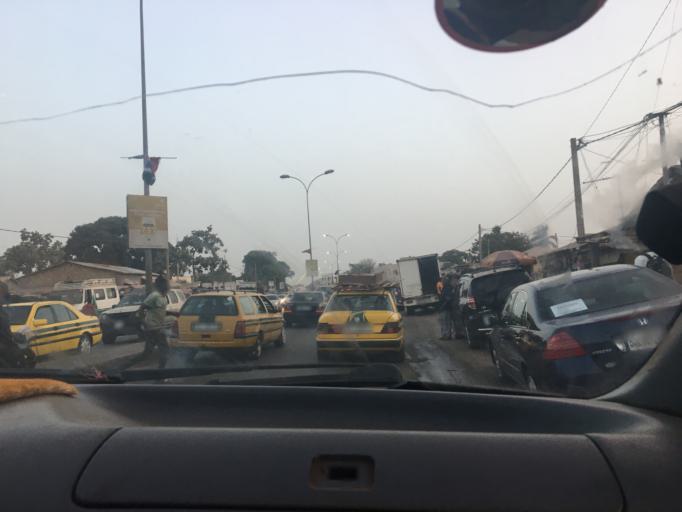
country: GM
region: Banjul
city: Bakau
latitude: 13.4396
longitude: -16.6767
